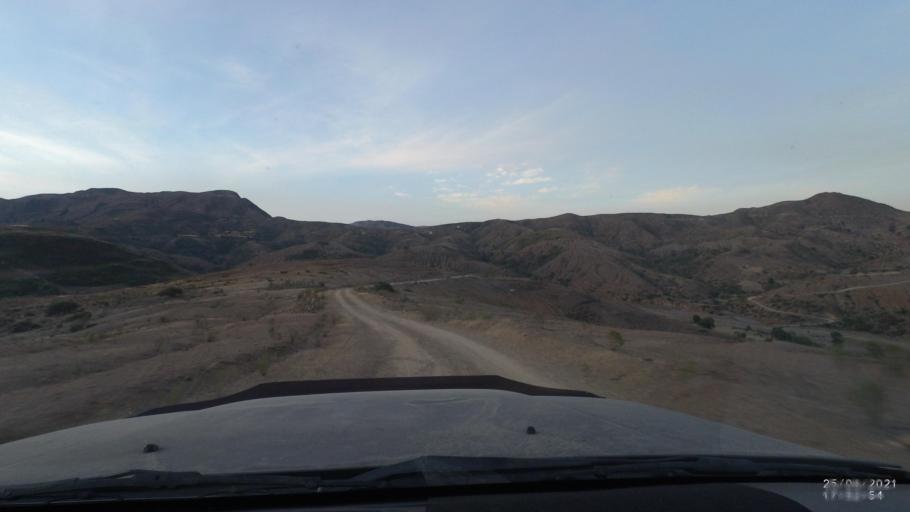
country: BO
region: Cochabamba
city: Mizque
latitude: -17.9449
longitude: -65.6394
